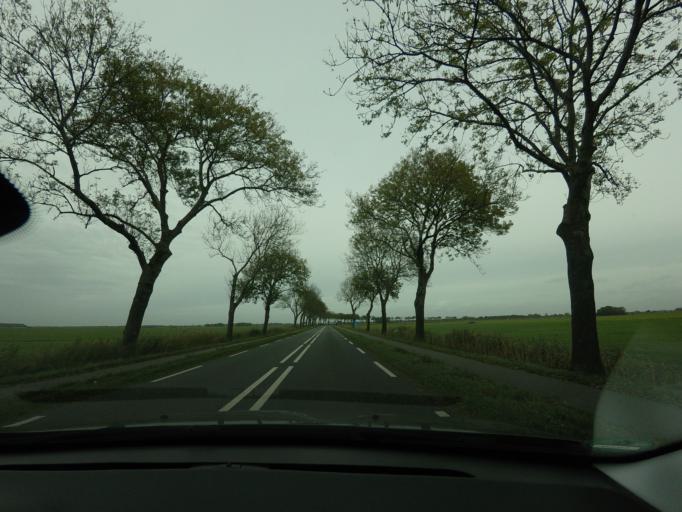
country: NL
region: Overijssel
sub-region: Gemeente Steenwijkerland
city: Blokzijl
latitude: 52.7318
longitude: 5.9587
